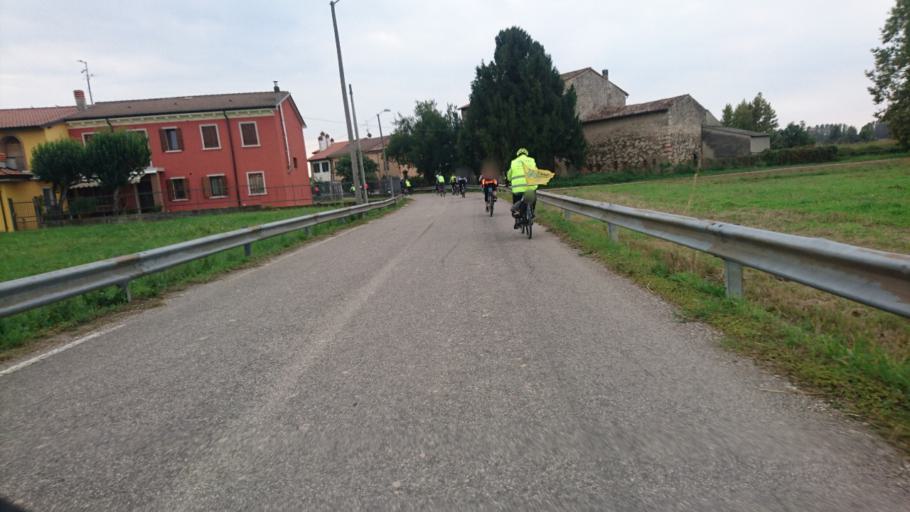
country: IT
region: Veneto
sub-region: Provincia di Verona
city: San Giovanni Lupatoto
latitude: 45.4085
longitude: 11.0582
